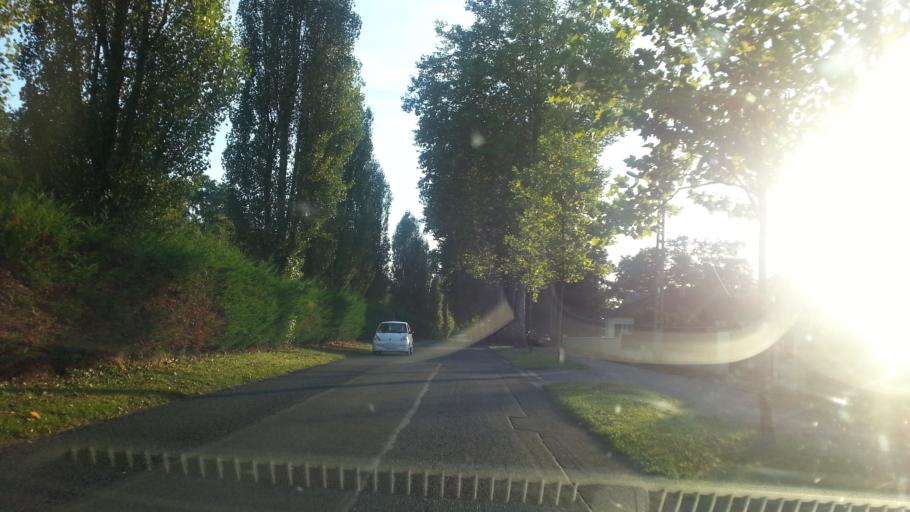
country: FR
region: Picardie
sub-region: Departement de l'Oise
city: Venette
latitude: 49.3976
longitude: 2.8100
